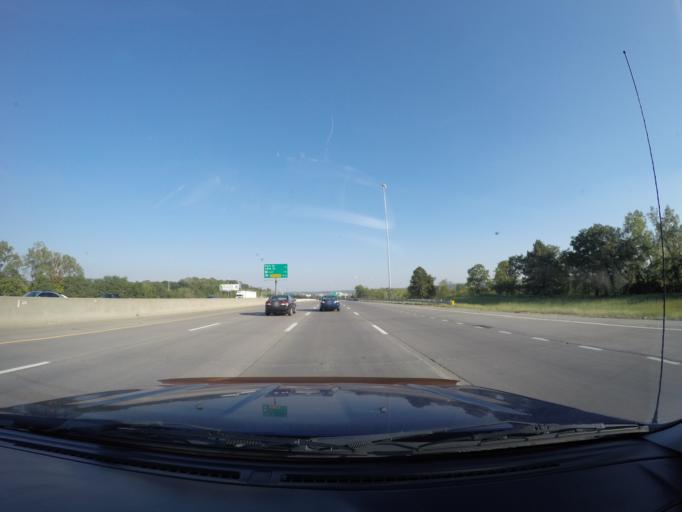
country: US
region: Kansas
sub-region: Wyandotte County
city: Kansas City
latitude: 39.1020
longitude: -94.6732
